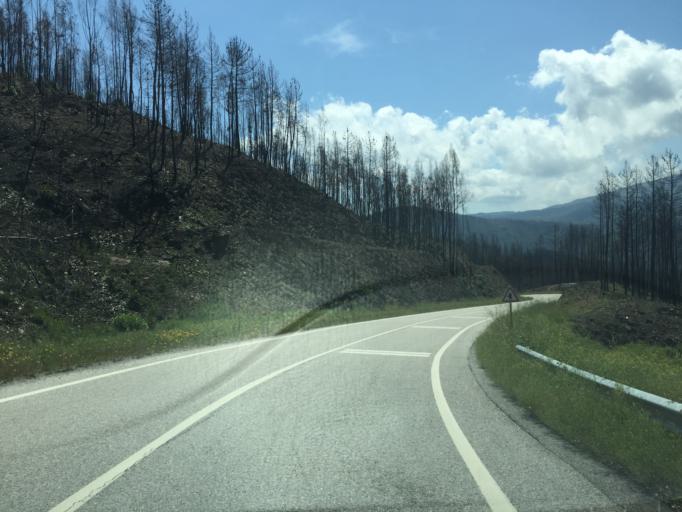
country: PT
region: Coimbra
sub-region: Pampilhosa da Serra
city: Pampilhosa da Serra
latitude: 39.9932
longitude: -7.9716
